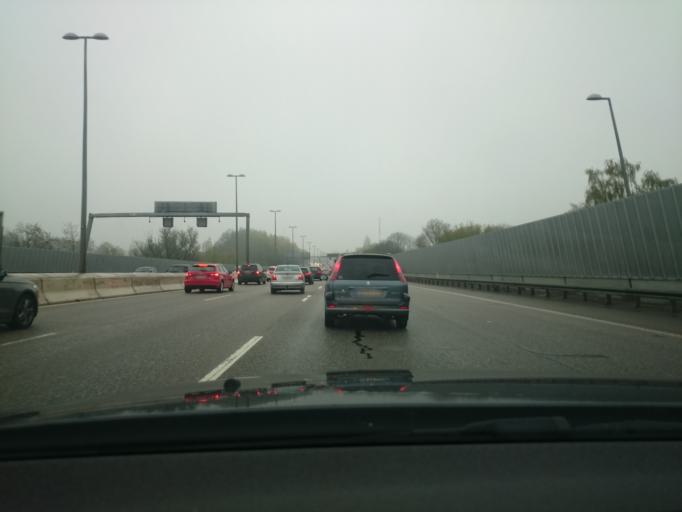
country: DK
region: Capital Region
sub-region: Herlev Kommune
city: Herlev
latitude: 55.7147
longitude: 12.4531
